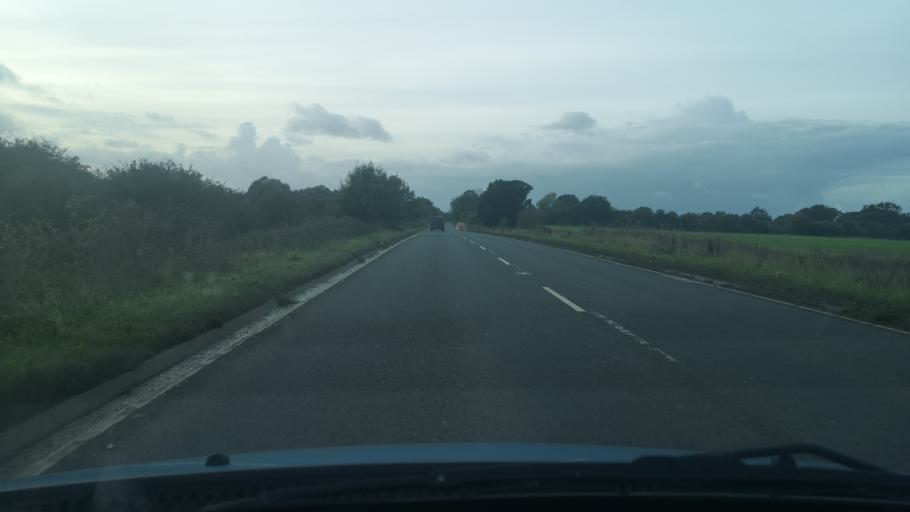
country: GB
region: England
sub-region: North Lincolnshire
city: Belton
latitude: 53.5822
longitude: -0.8025
